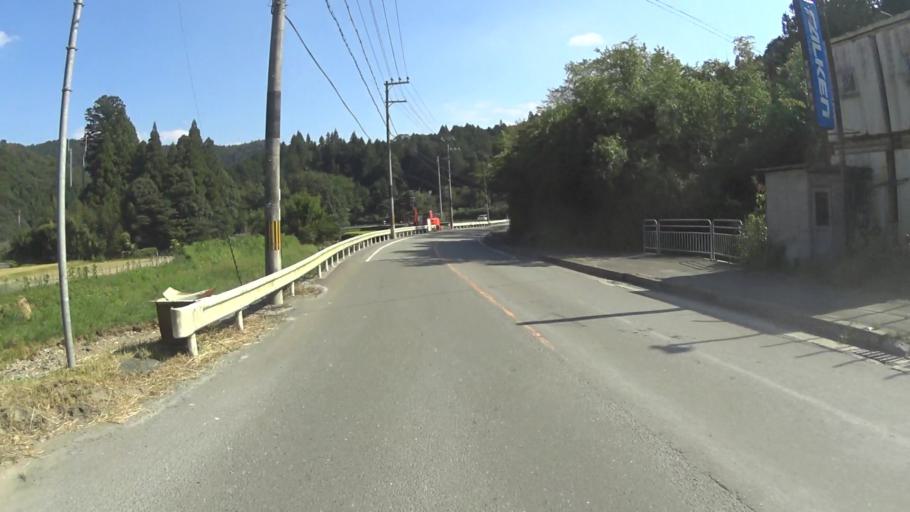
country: JP
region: Kyoto
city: Kameoka
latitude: 34.9309
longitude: 135.5576
